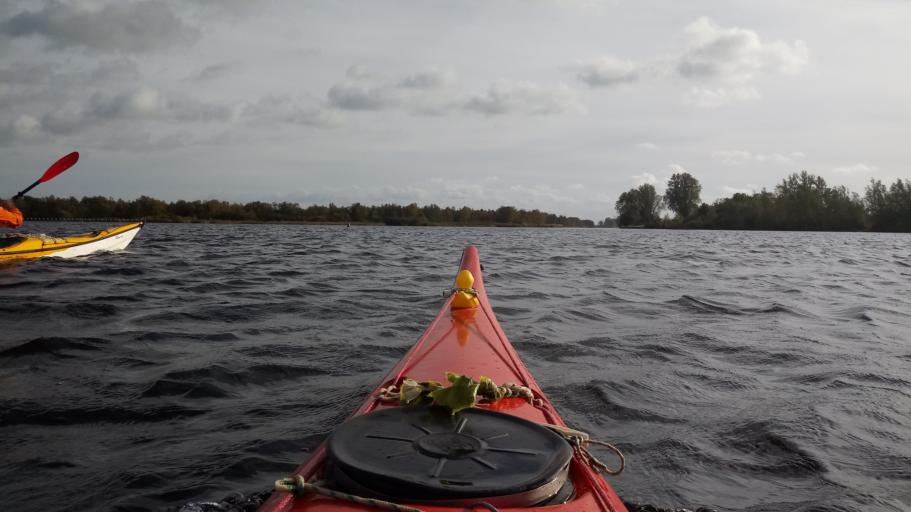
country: NL
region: Overijssel
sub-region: Gemeente Steenwijkerland
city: Wanneperveen
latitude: 52.6820
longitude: 6.0883
